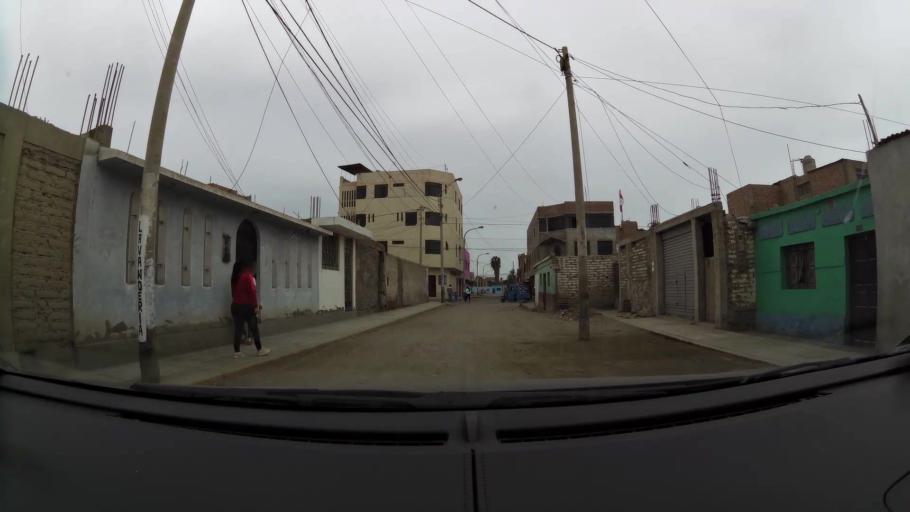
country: PE
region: Lima
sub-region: Barranca
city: Barranca
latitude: -10.7468
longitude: -77.7549
